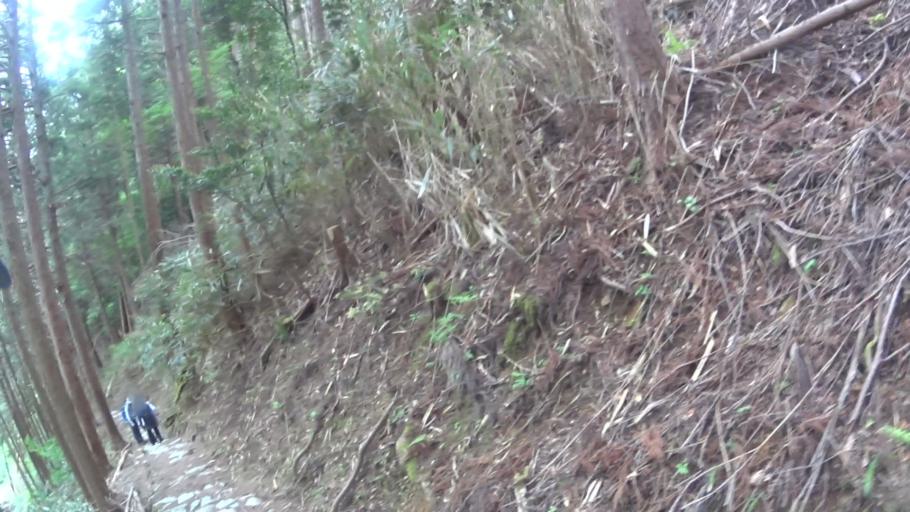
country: JP
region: Nara
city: Yoshino-cho
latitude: 34.3404
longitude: 135.8802
